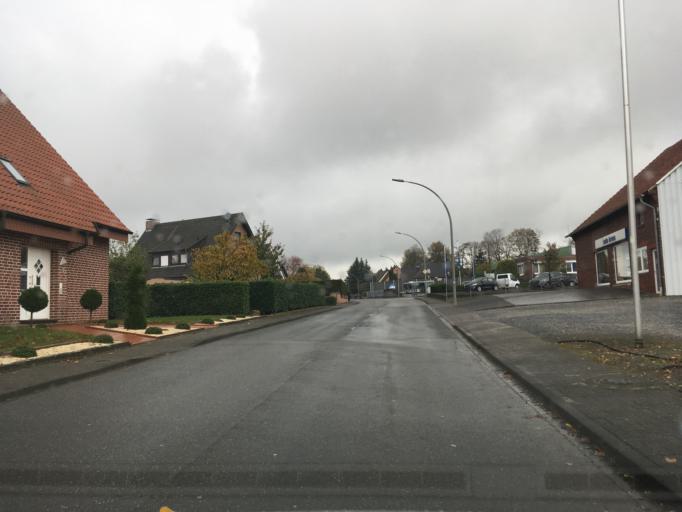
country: DE
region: North Rhine-Westphalia
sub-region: Regierungsbezirk Munster
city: Klein Reken
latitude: 51.8331
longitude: 7.0397
